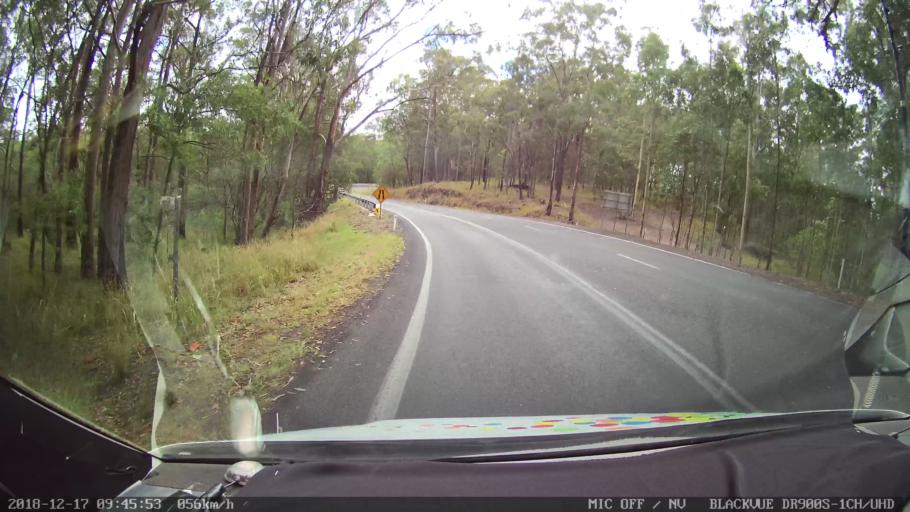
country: AU
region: New South Wales
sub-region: Tenterfield Municipality
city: Carrolls Creek
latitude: -28.9251
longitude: 152.3335
